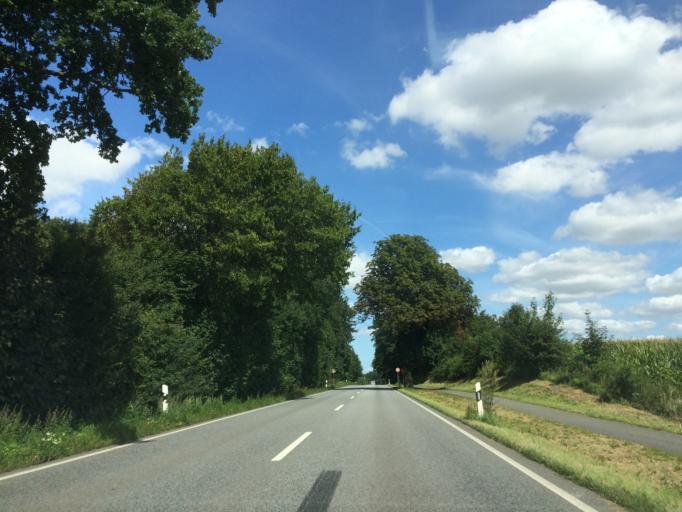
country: DE
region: Schleswig-Holstein
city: Grebin
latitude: 54.1988
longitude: 10.4703
